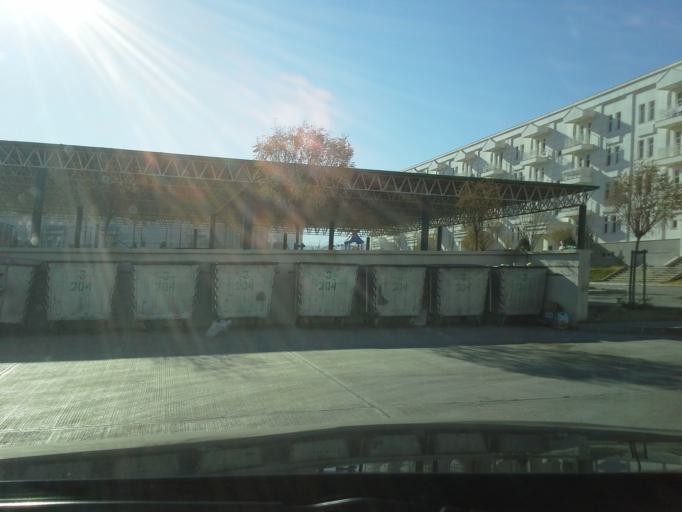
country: TM
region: Ahal
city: Ashgabat
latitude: 37.9719
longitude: 58.3379
